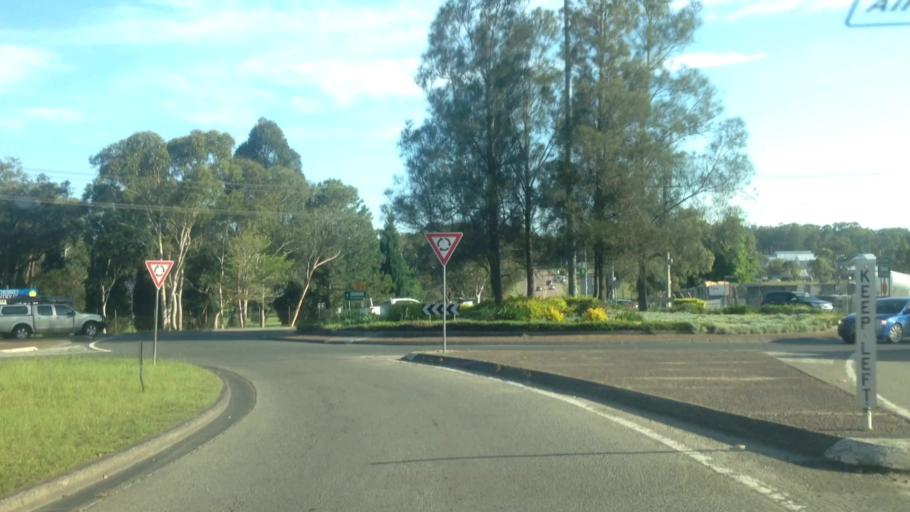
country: AU
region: New South Wales
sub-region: Lake Macquarie Shire
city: Dora Creek
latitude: -33.1125
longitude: 151.4782
